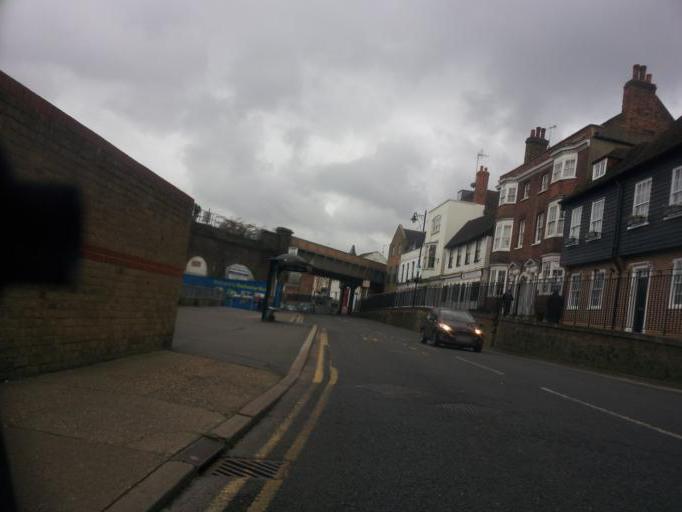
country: GB
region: England
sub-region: Medway
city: Rochester
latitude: 51.3842
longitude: 0.5114
